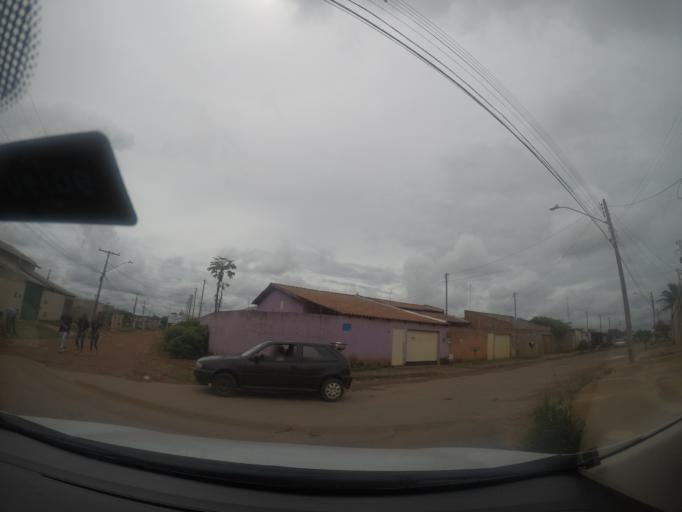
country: BR
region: Goias
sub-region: Trindade
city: Trindade
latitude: -16.6905
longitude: -49.4035
